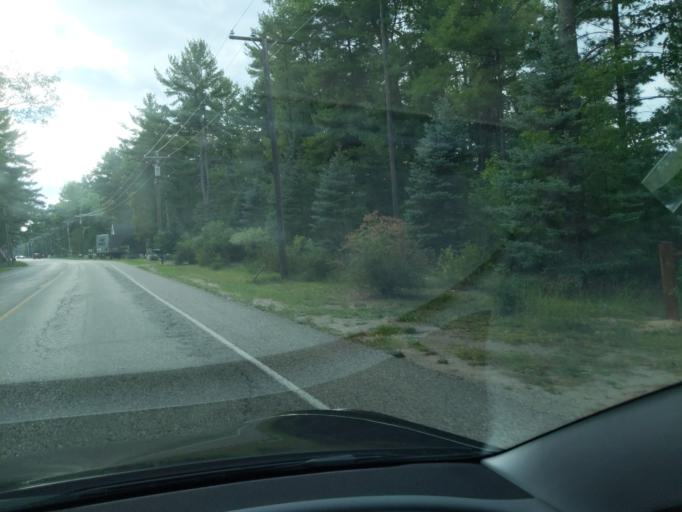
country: US
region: Michigan
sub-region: Kalkaska County
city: Rapid City
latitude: 44.8563
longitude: -85.3014
